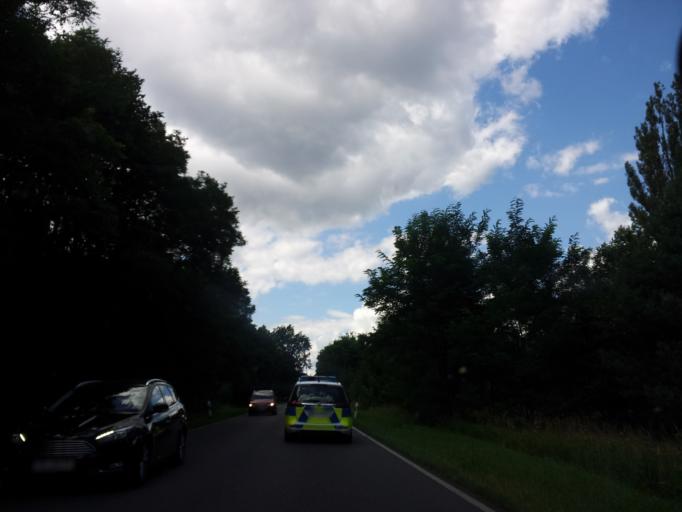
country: DE
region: Brandenburg
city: Niedergorsdorf
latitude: 52.0200
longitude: 12.9872
